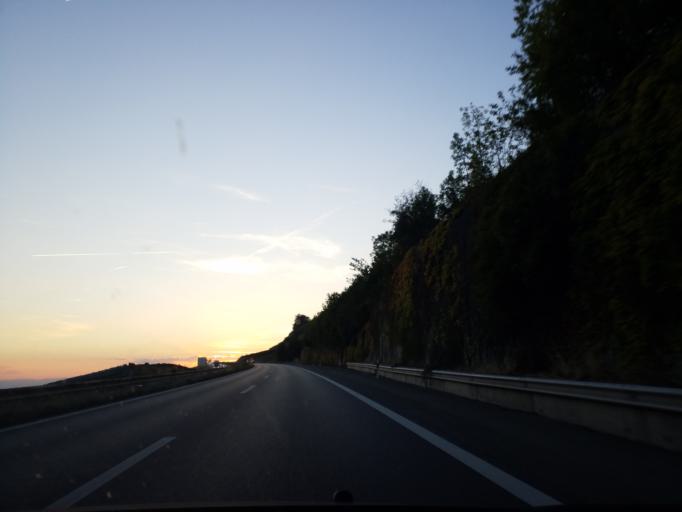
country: CH
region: Vaud
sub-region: Riviera-Pays-d'Enhaut District
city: Chardonne
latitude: 46.4751
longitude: 6.8168
